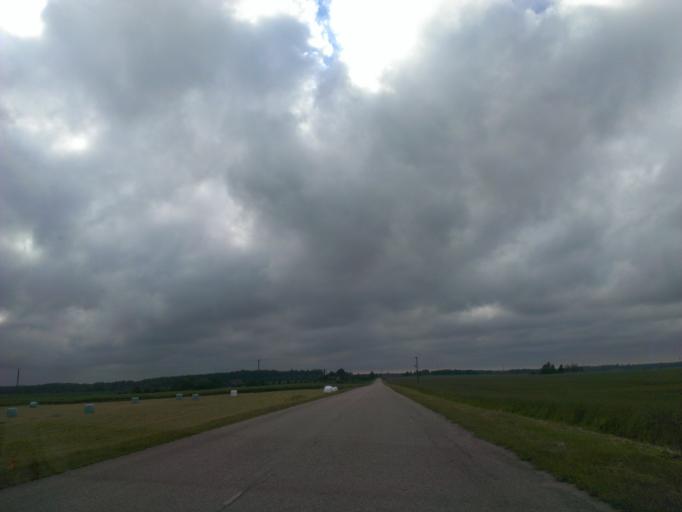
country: LV
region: Aizpute
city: Aizpute
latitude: 56.7140
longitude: 21.4713
